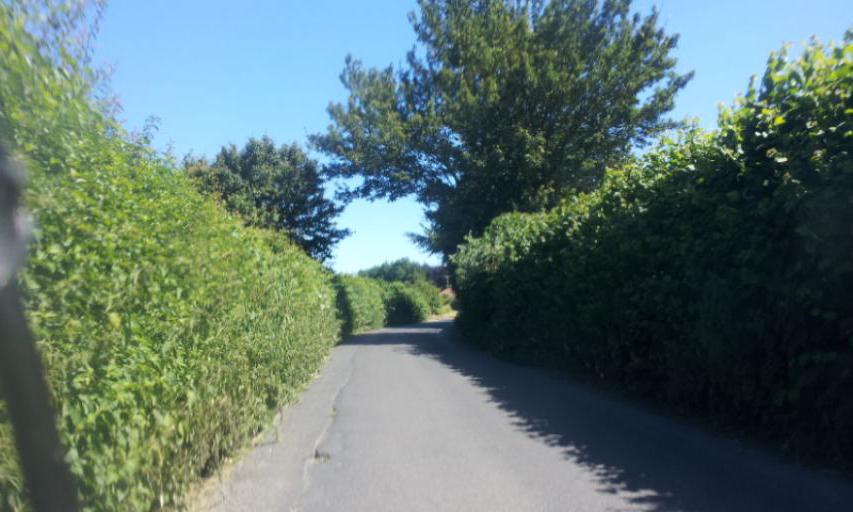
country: GB
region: England
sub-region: Kent
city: Sittingbourne
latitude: 51.3056
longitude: 0.7123
